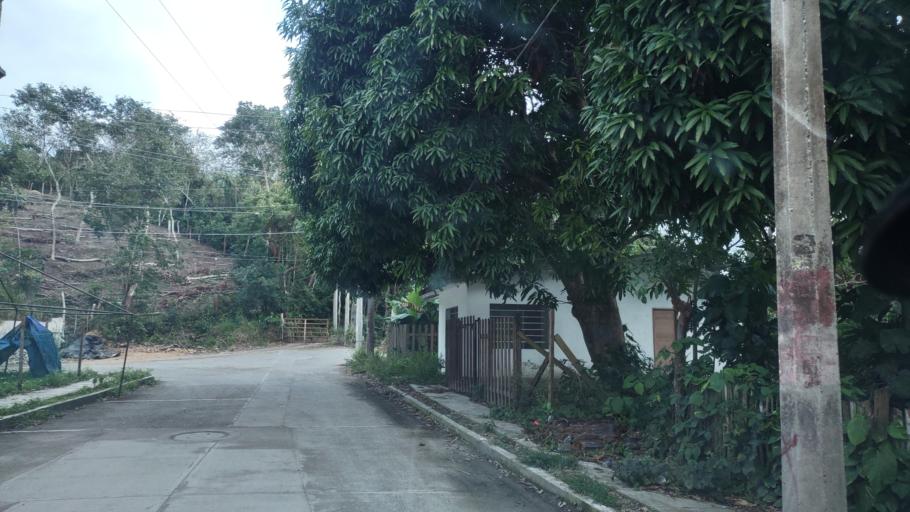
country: MX
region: Veracruz
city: Papantla de Olarte
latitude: 20.4545
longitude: -97.3064
